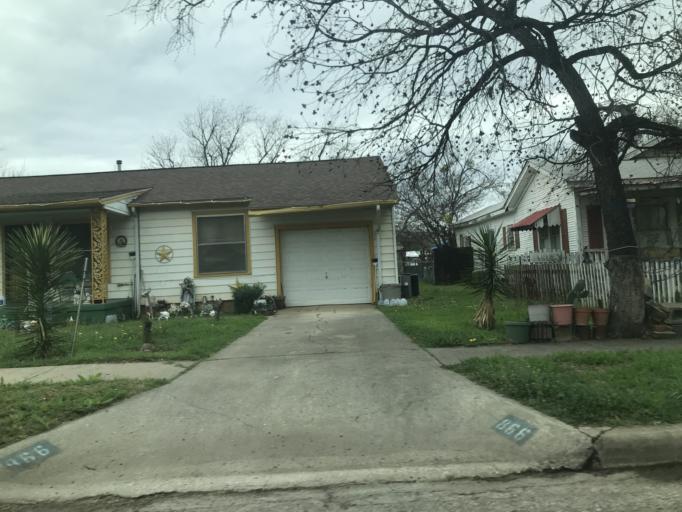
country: US
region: Texas
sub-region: Taylor County
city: Abilene
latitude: 32.4590
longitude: -99.7454
